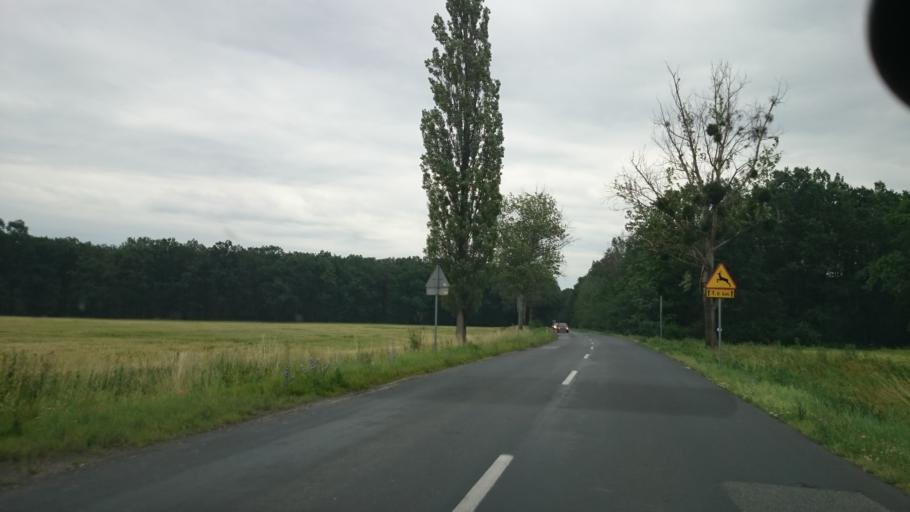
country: PL
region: Opole Voivodeship
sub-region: Powiat brzeski
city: Grodkow
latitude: 50.6685
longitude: 17.4180
